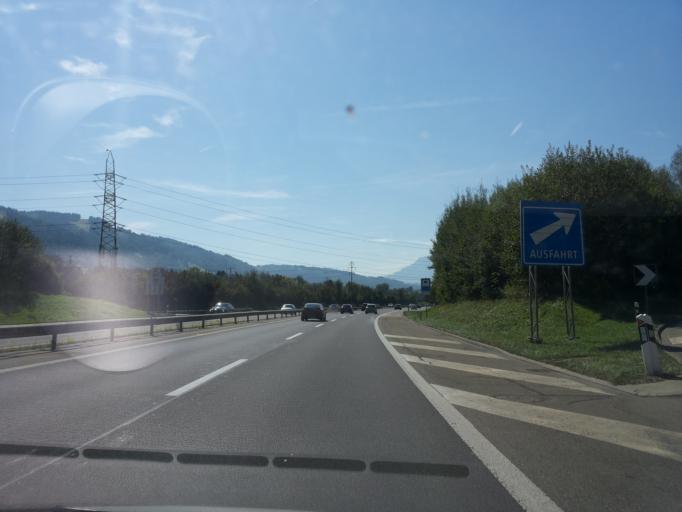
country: CH
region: Lucerne
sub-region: Lucerne-Land District
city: Root
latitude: 47.1243
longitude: 8.3936
